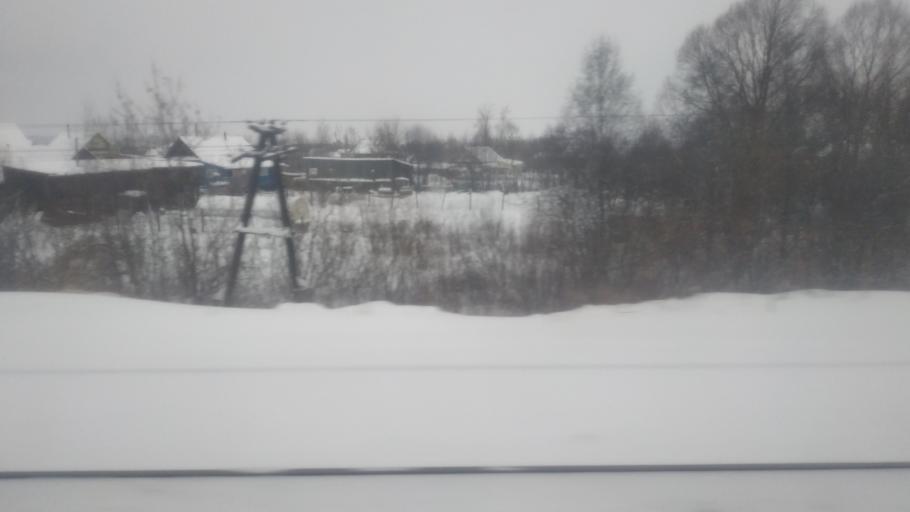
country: RU
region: Bashkortostan
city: Yanaul
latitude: 56.2771
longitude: 54.9457
